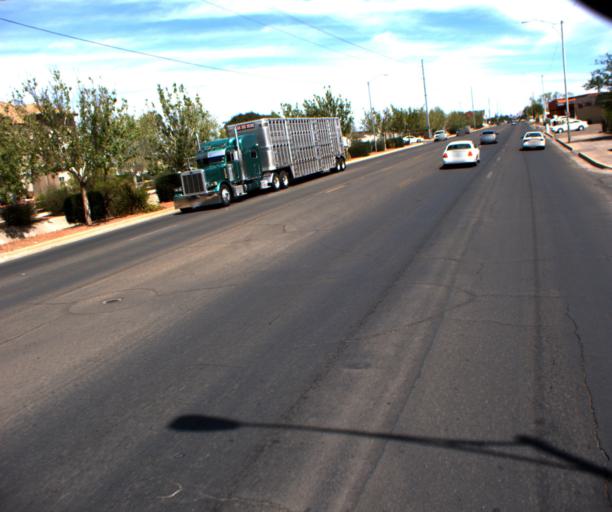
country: US
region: Arizona
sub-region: Cochise County
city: Douglas
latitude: 31.3402
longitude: -109.5585
